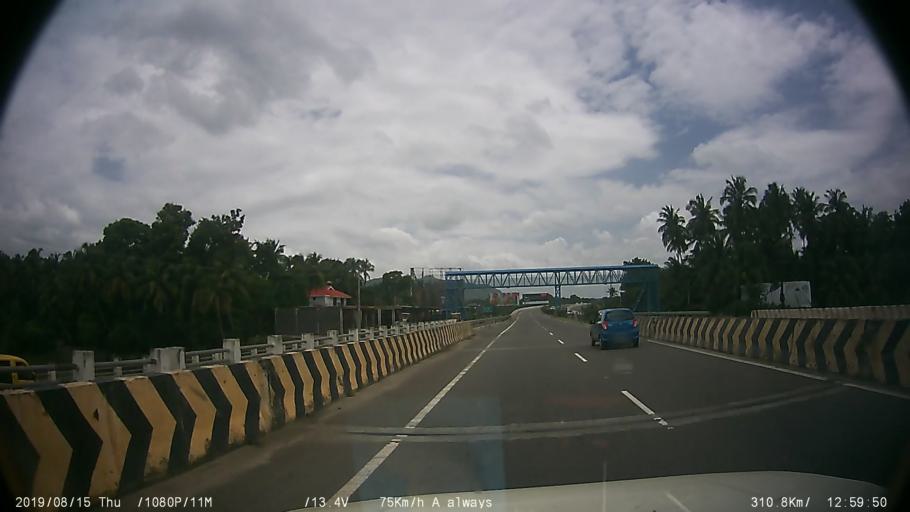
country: IN
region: Kerala
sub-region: Palakkad district
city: Palakkad
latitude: 10.6487
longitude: 76.5625
